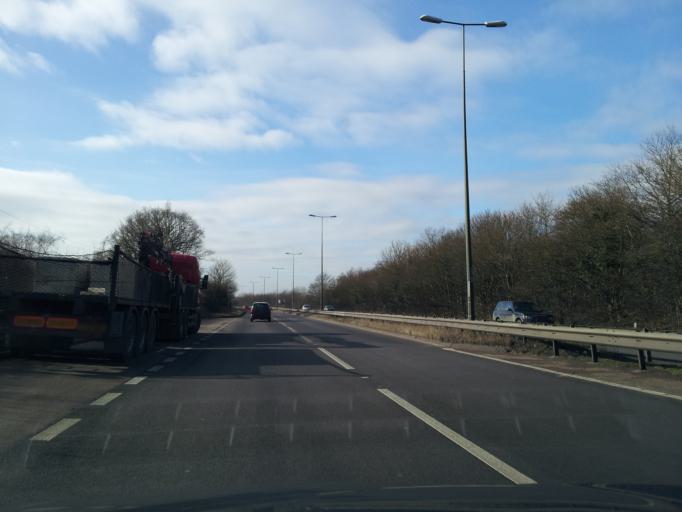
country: GB
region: England
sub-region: Derbyshire
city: Long Eaton
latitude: 52.9140
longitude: -1.3140
